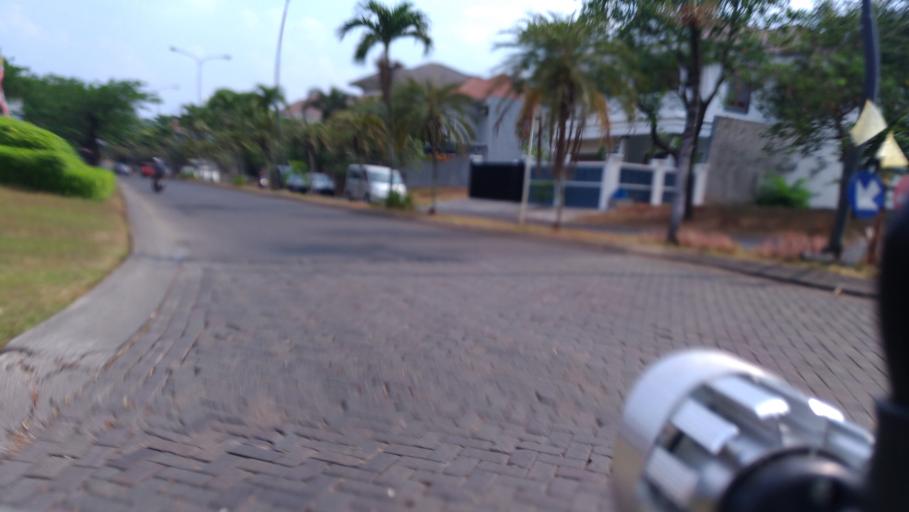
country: ID
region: West Java
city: Cileungsir
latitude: -6.3972
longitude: 106.9435
